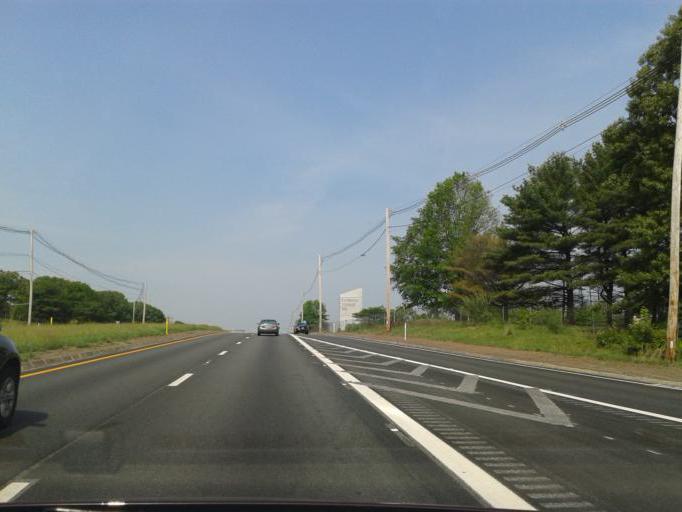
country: US
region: Massachusetts
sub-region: Worcester County
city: Southborough
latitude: 42.2888
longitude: -71.5707
